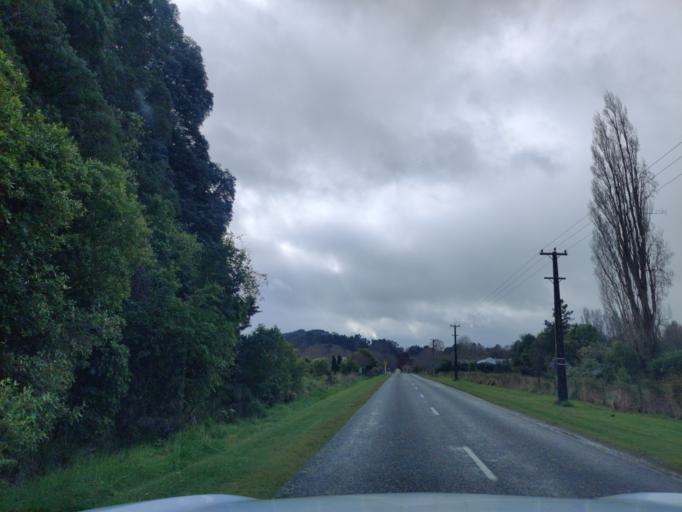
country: NZ
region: Manawatu-Wanganui
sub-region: Palmerston North City
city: Palmerston North
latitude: -40.1753
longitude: 175.7925
